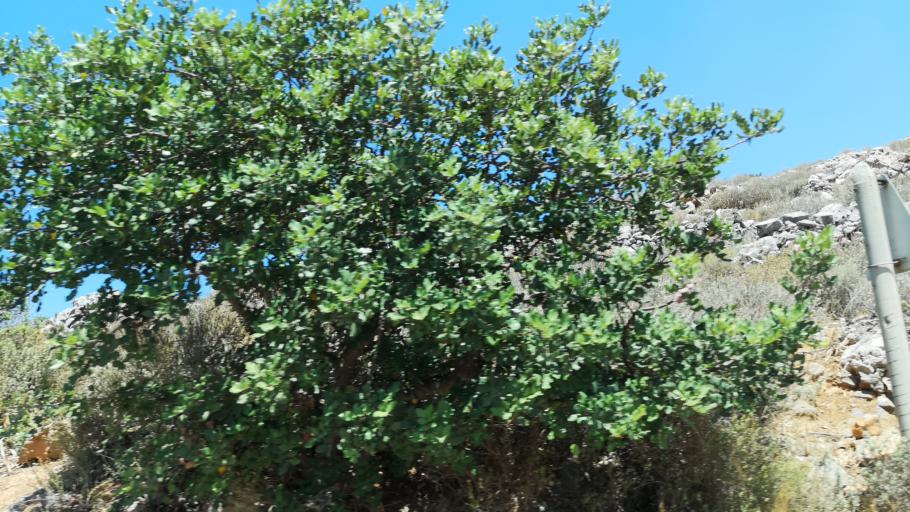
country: GR
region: Crete
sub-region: Nomos Lasithiou
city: Neapoli
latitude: 35.2529
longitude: 25.6318
